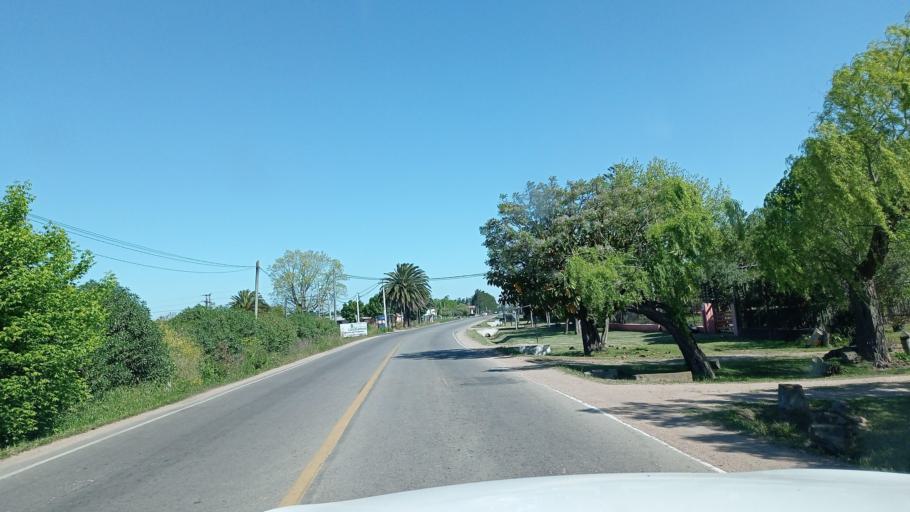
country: UY
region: Canelones
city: La Paz
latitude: -34.7869
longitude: -56.1665
